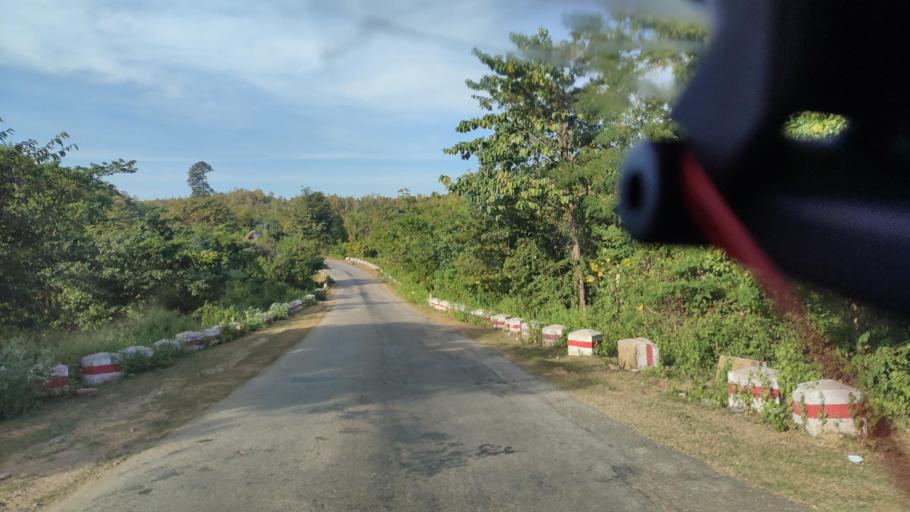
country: MM
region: Magway
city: Taungdwingyi
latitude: 19.9925
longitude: 95.8892
